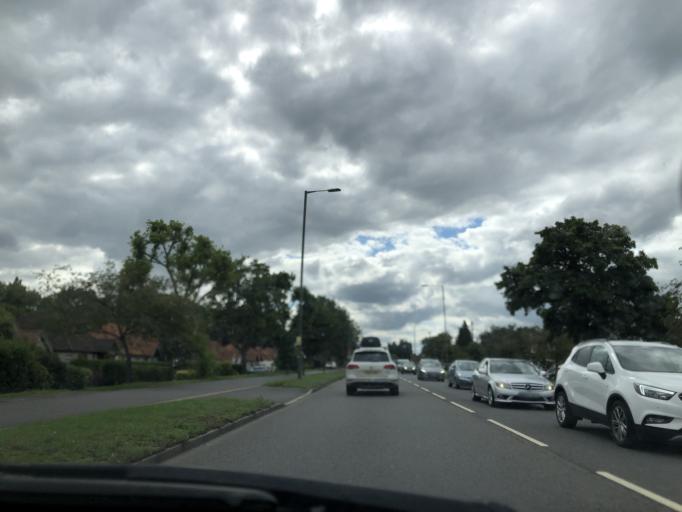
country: GB
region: England
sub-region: Greater London
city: Sidcup
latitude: 51.4047
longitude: 0.1132
